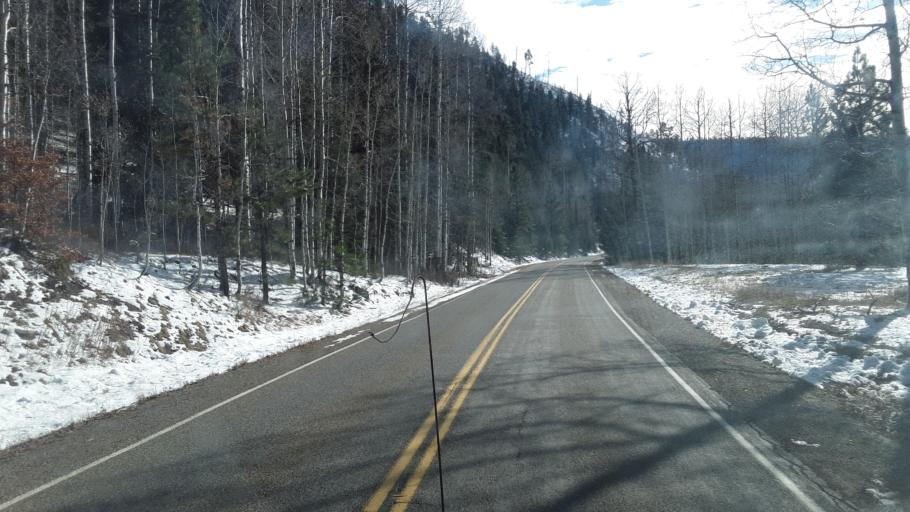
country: US
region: Colorado
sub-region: La Plata County
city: Bayfield
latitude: 37.3773
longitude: -107.6592
